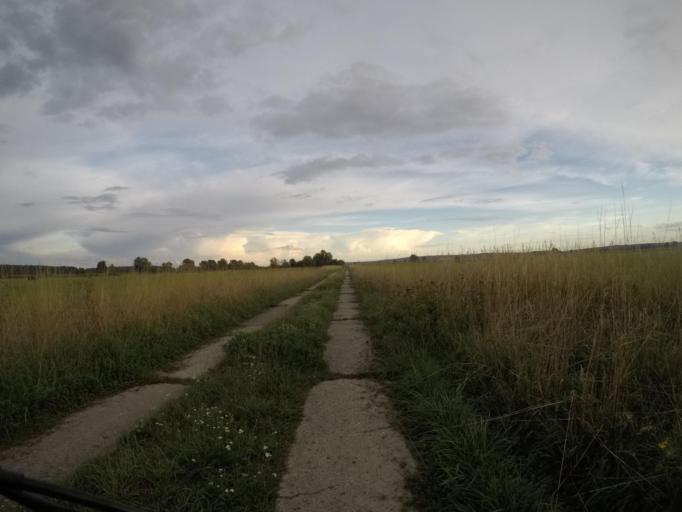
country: DE
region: Lower Saxony
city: Neu Darchau
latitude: 53.2693
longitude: 10.8946
